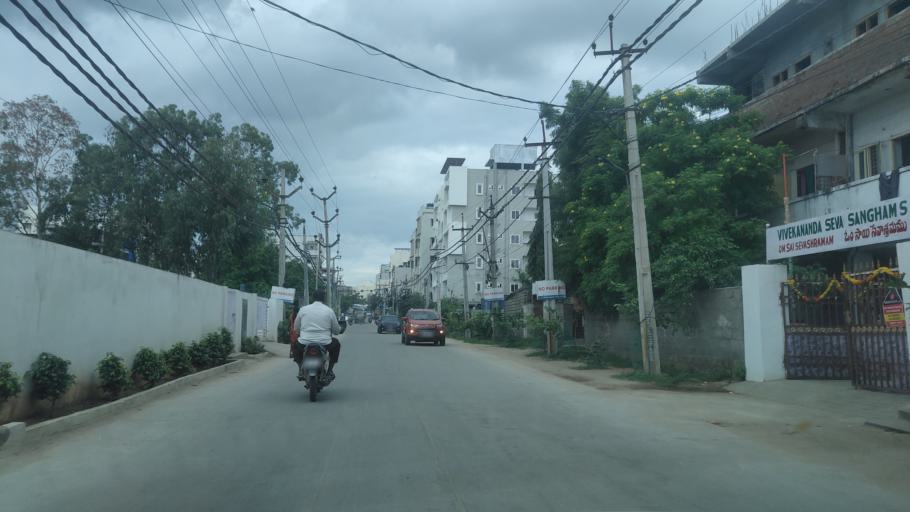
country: IN
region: Telangana
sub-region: Medak
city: Serilingampalle
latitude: 17.4974
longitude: 78.3487
